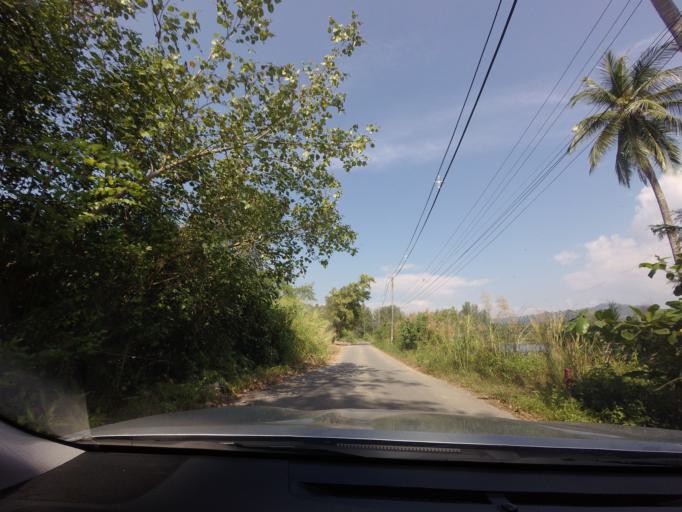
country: TH
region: Phangnga
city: Ban Khao Lak
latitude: 8.7310
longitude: 98.2416
